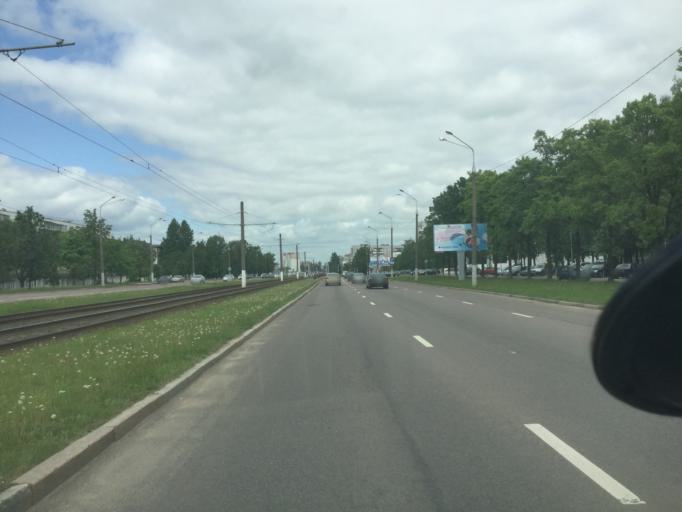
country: BY
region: Vitebsk
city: Vitebsk
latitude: 55.1807
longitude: 30.2298
